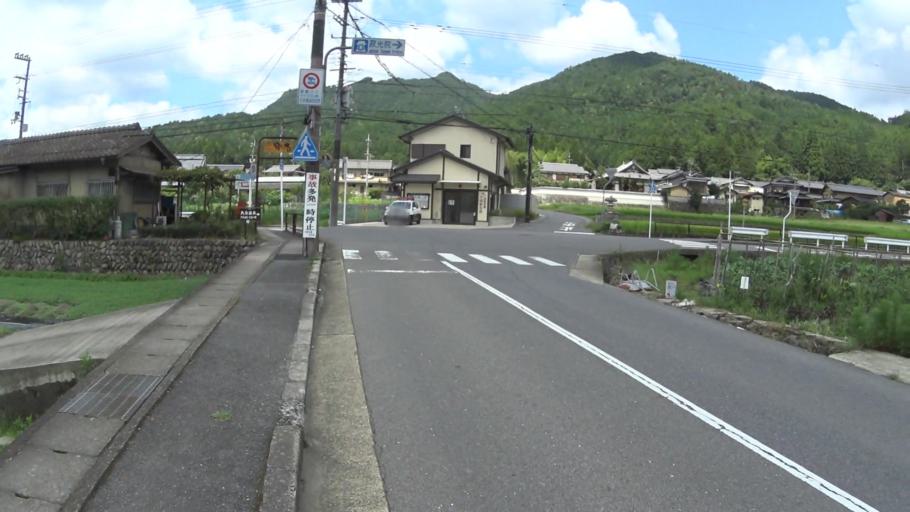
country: JP
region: Kyoto
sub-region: Kyoto-shi
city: Kamigyo-ku
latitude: 35.1135
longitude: 135.8228
